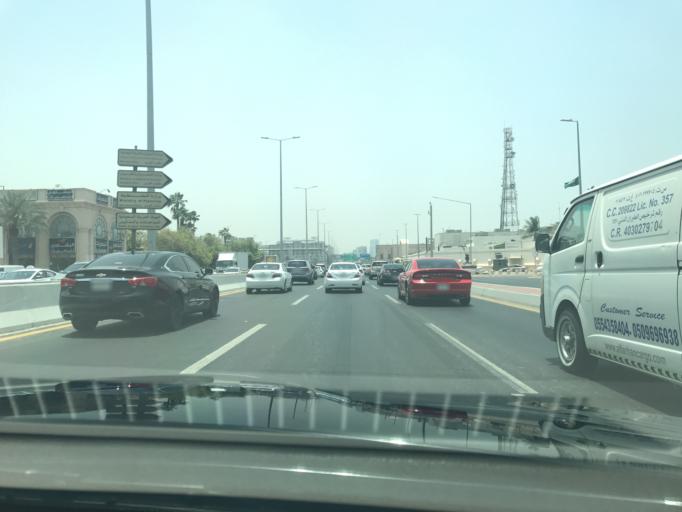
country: SA
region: Makkah
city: Jeddah
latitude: 21.5354
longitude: 39.1781
